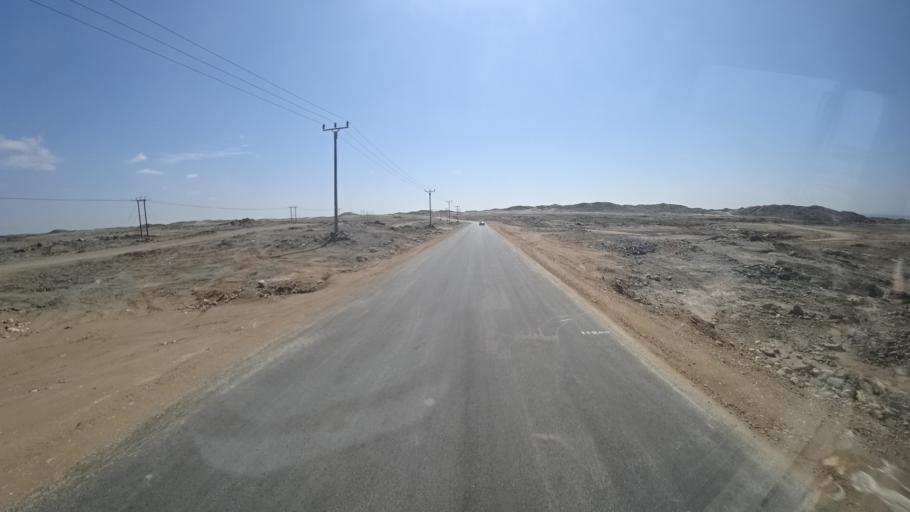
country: OM
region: Zufar
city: Salalah
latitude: 16.9658
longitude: 54.7553
